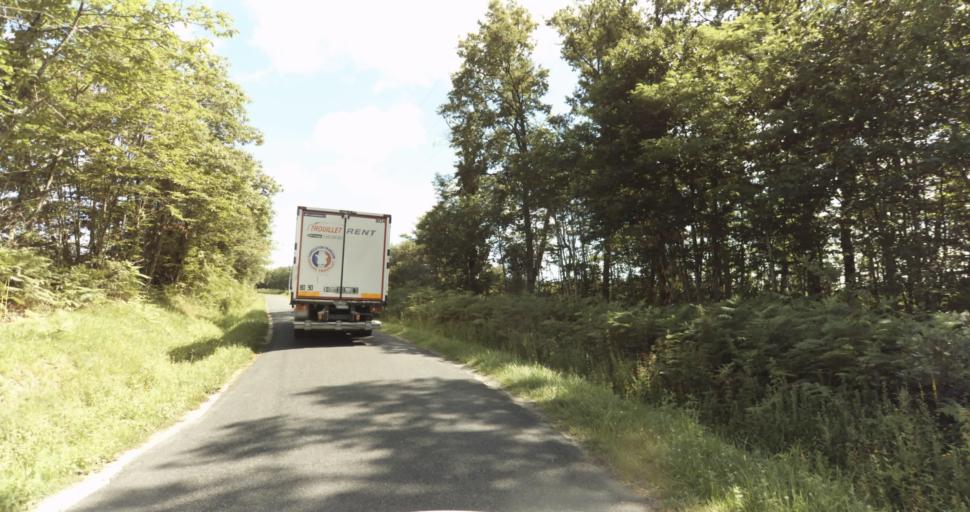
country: FR
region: Aquitaine
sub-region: Departement de la Gironde
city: Bazas
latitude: 44.4508
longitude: -0.2180
